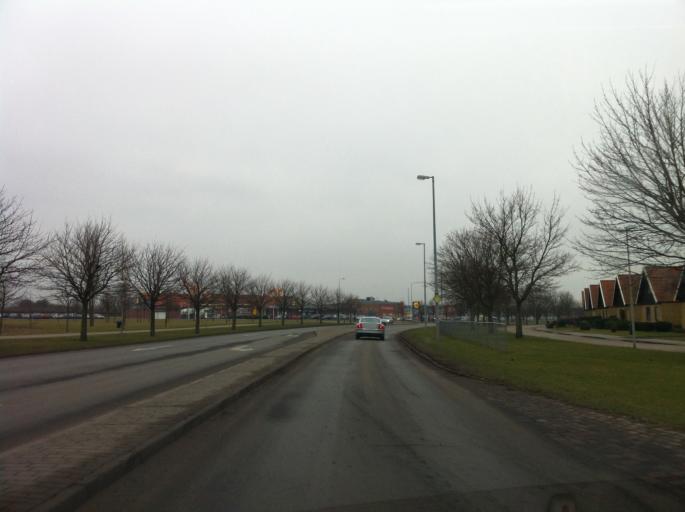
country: SE
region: Skane
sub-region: Landskrona
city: Landskrona
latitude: 55.8818
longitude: 12.8517
